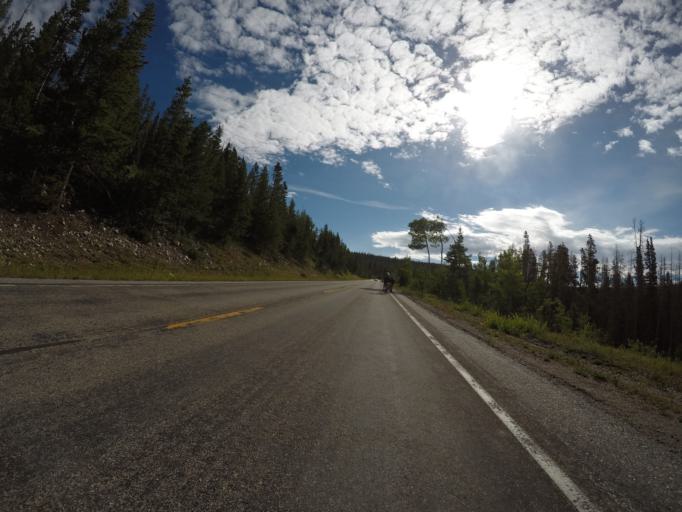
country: US
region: Wyoming
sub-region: Carbon County
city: Saratoga
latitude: 41.3285
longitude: -106.4830
